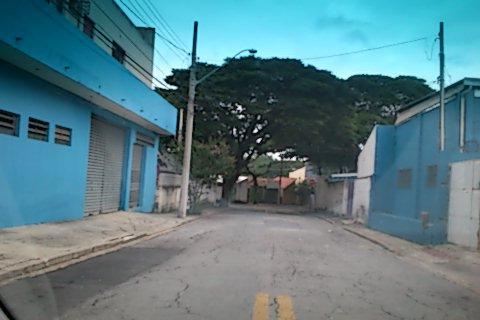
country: BR
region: Sao Paulo
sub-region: Sao Jose Dos Campos
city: Sao Jose dos Campos
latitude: -23.1973
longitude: -45.8768
